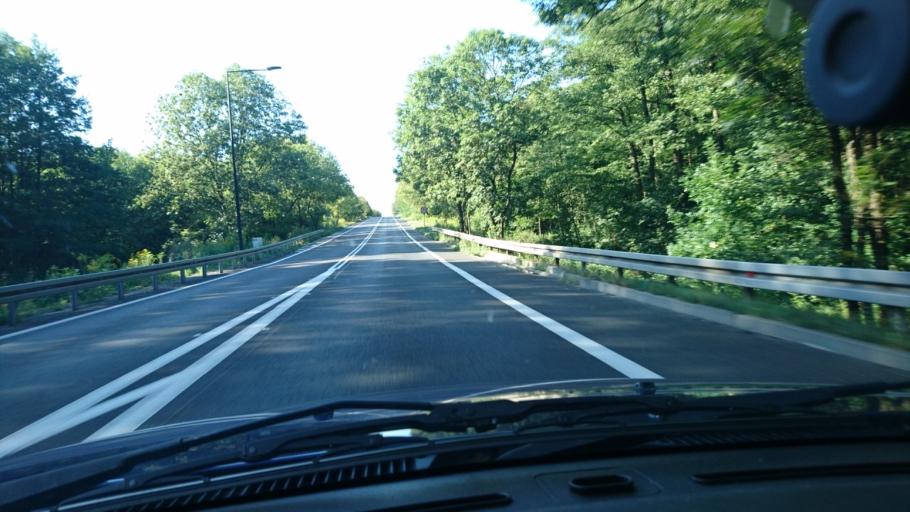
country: PL
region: Silesian Voivodeship
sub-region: Powiat gliwicki
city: Pyskowice
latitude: 50.3542
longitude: 18.6449
